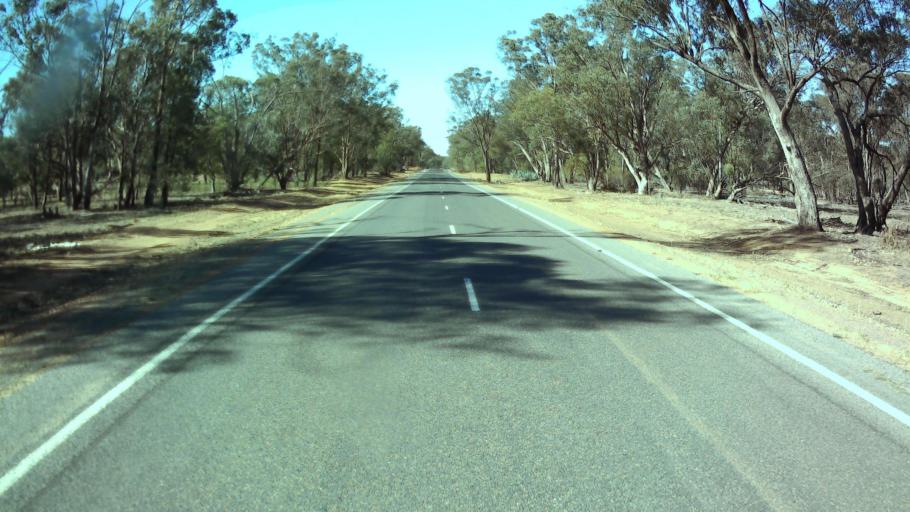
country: AU
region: New South Wales
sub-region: Weddin
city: Grenfell
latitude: -33.7533
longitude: 148.0836
